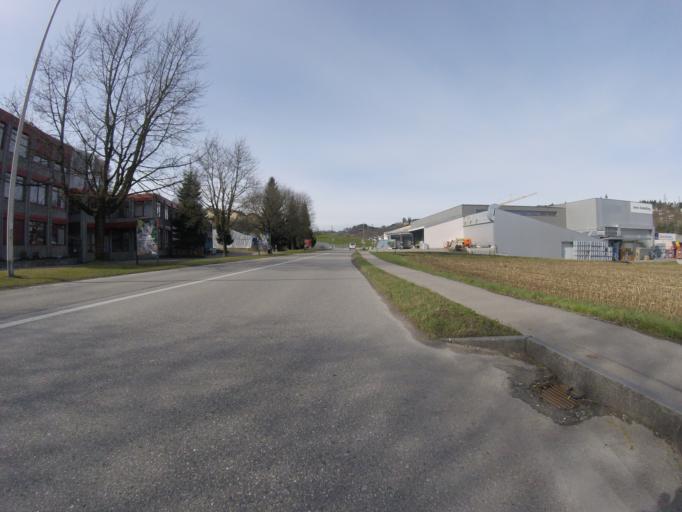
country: CH
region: Bern
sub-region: Bern-Mittelland District
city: Koniz
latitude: 46.9217
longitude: 7.3733
